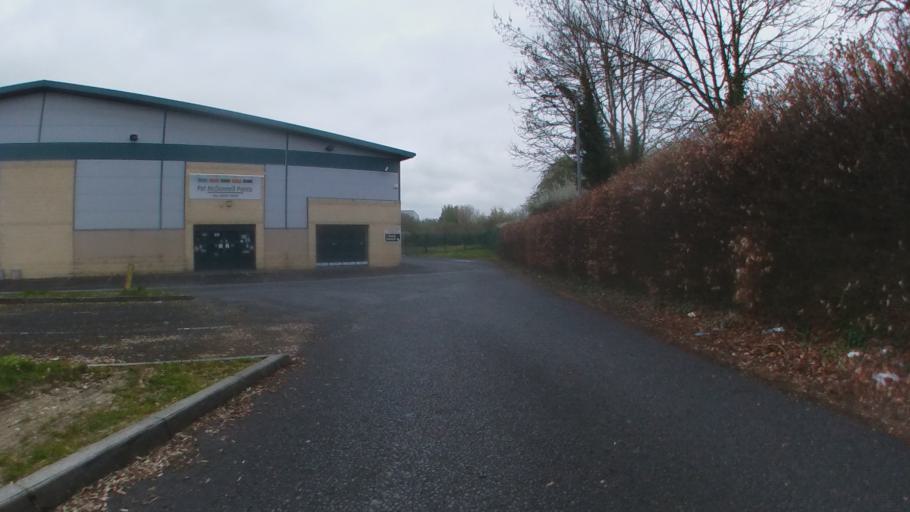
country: IE
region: Leinster
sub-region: Kilkenny
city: Kilkenny
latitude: 52.6459
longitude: -7.2202
